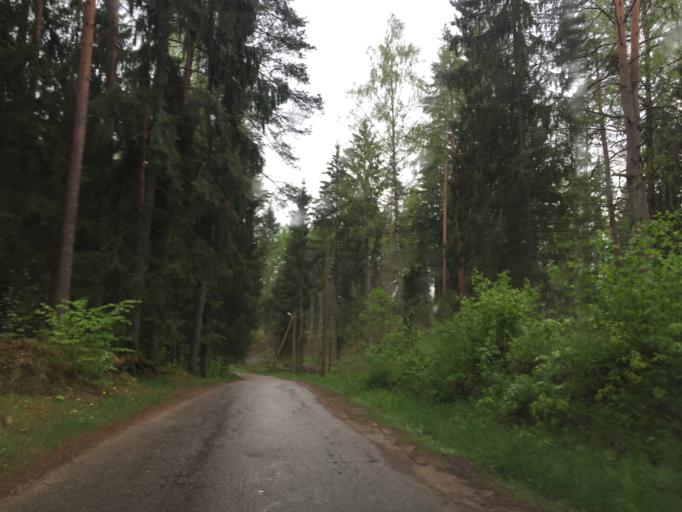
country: LV
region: Kegums
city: Kegums
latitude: 56.7400
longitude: 24.7349
